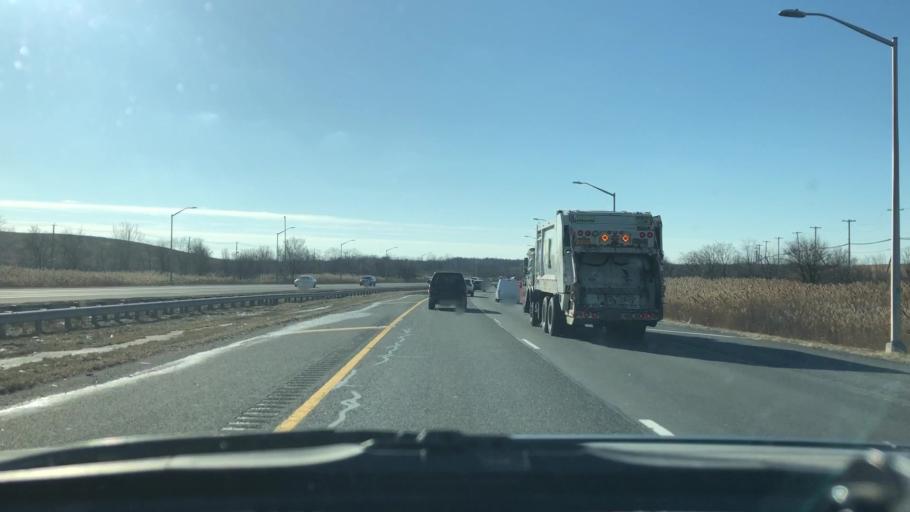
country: US
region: New Jersey
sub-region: Middlesex County
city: Carteret
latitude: 40.5751
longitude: -74.1903
